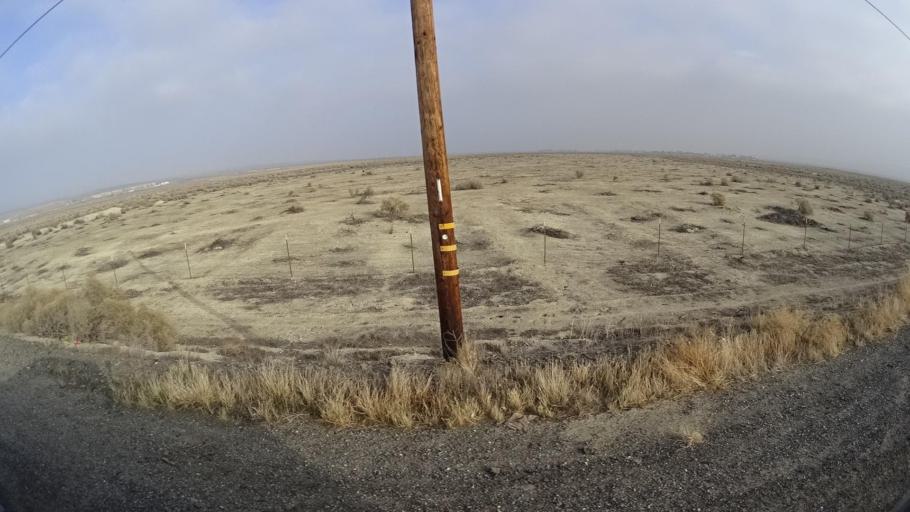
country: US
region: California
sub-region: Kern County
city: Ford City
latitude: 35.2221
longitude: -119.4456
